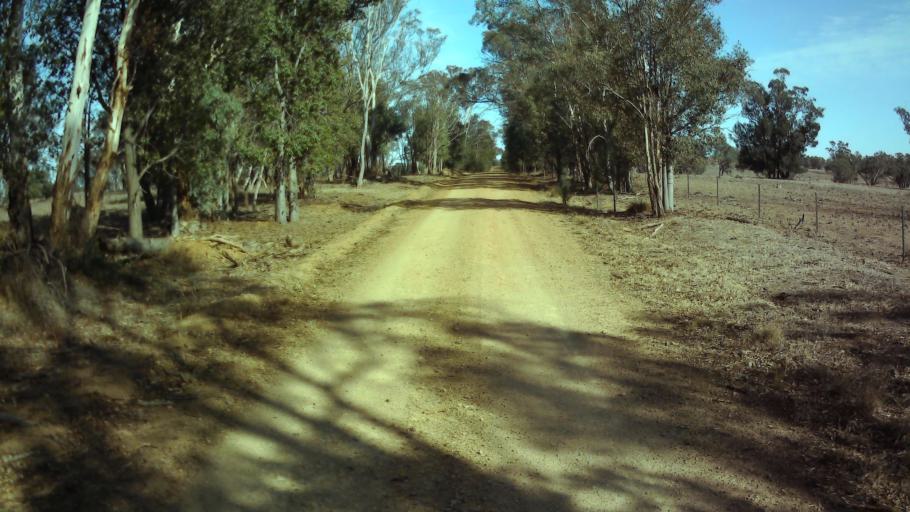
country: AU
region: New South Wales
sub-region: Weddin
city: Grenfell
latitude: -33.7590
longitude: 148.0298
